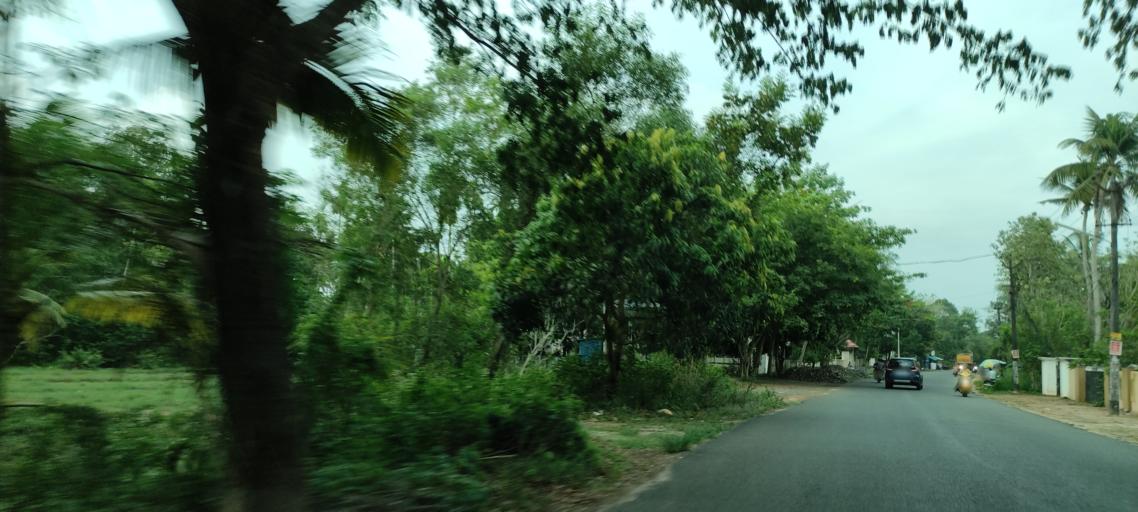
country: IN
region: Kerala
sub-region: Kottayam
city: Vaikam
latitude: 9.7309
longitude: 76.3619
